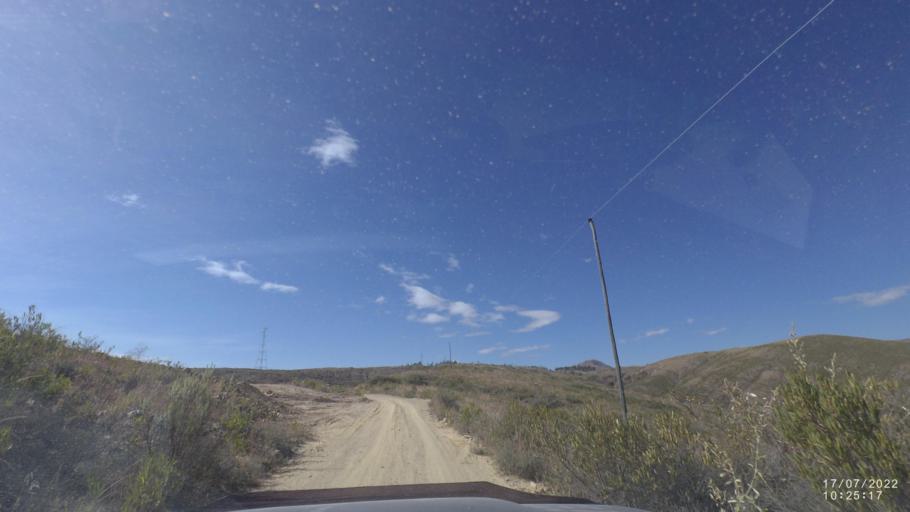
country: BO
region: Cochabamba
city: Capinota
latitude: -17.6172
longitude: -66.1729
